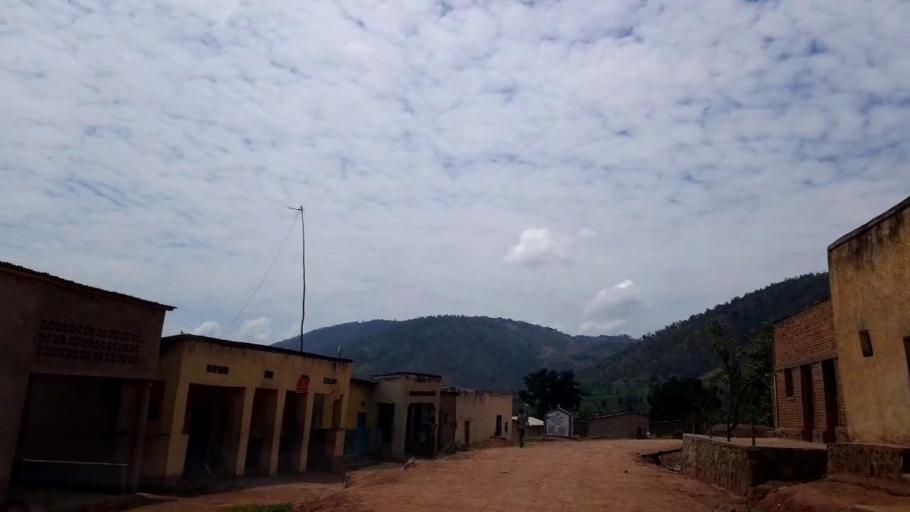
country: RW
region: Northern Province
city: Byumba
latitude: -1.4979
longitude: 30.1943
